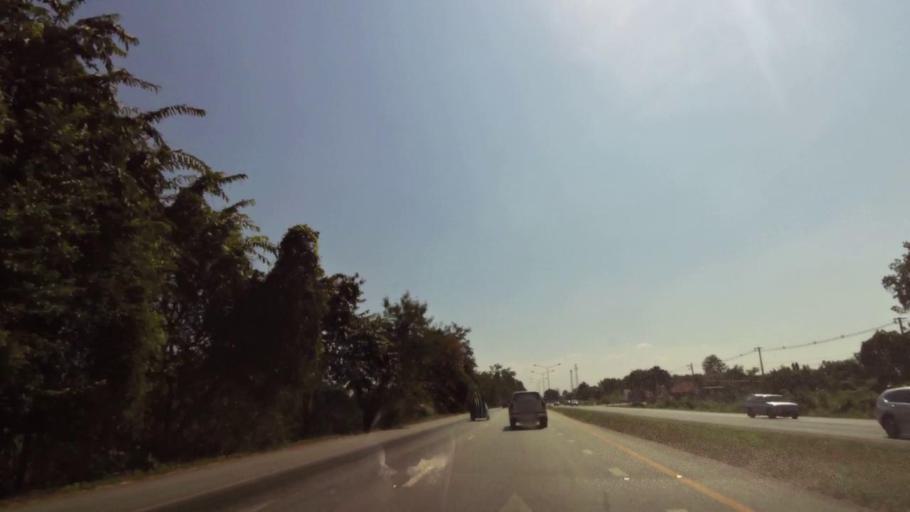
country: TH
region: Nakhon Sawan
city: Kao Liao
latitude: 15.8139
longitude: 100.1197
